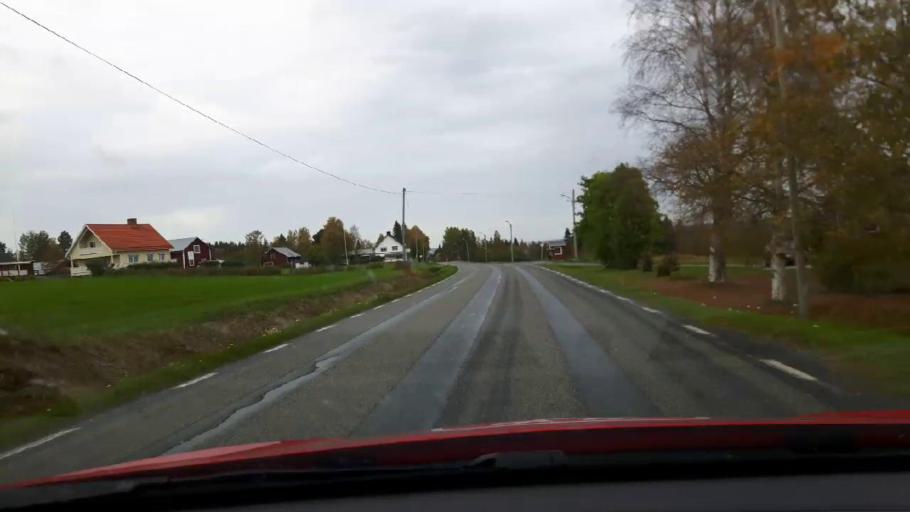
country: SE
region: Jaemtland
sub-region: Bergs Kommun
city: Hoverberg
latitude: 62.8542
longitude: 14.3812
